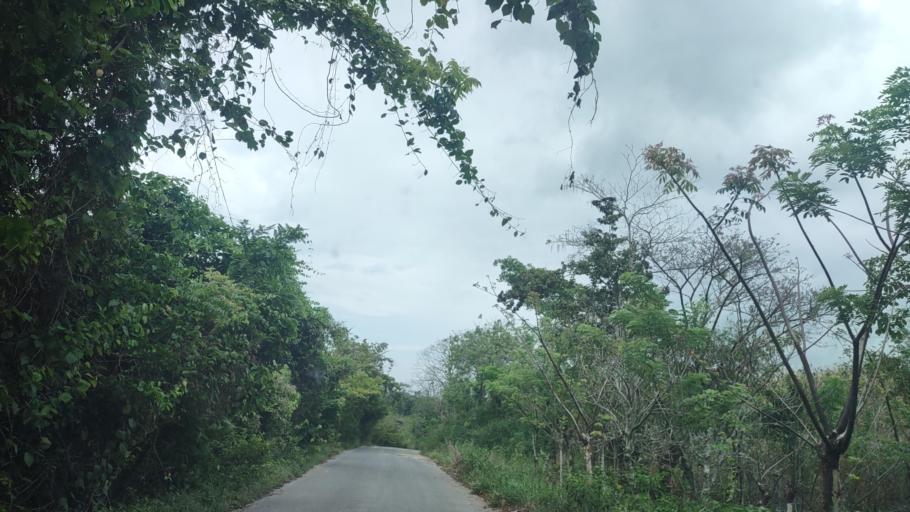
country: MX
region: Tabasco
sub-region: Huimanguillo
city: Francisco Rueda
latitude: 17.5245
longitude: -94.1319
